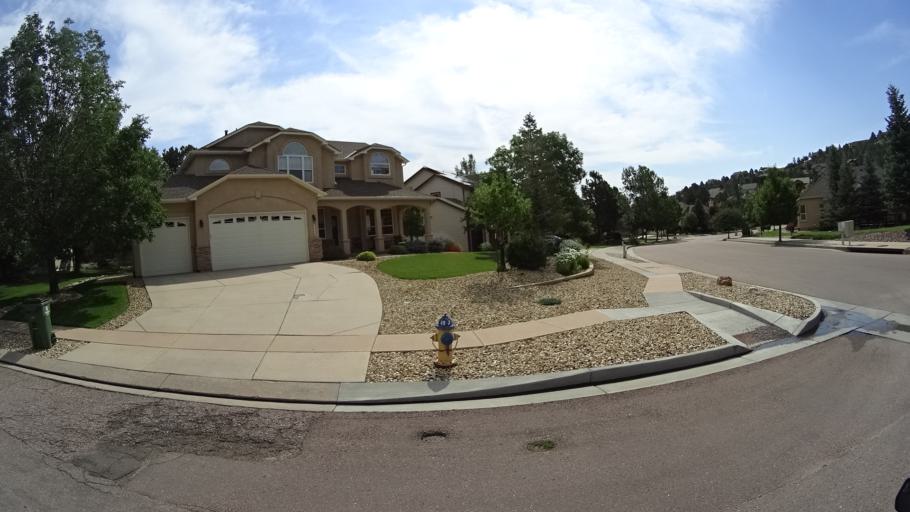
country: US
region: Colorado
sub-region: El Paso County
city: Air Force Academy
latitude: 38.9431
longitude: -104.8660
